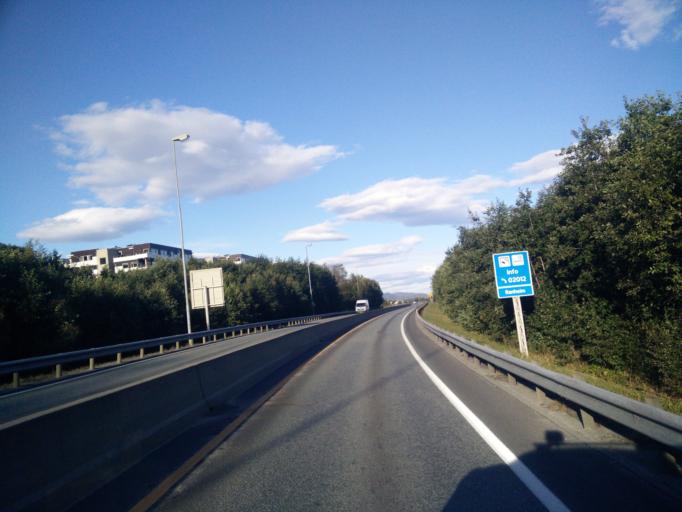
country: NO
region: Sor-Trondelag
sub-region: Malvik
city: Malvik
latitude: 63.4226
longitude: 10.5526
